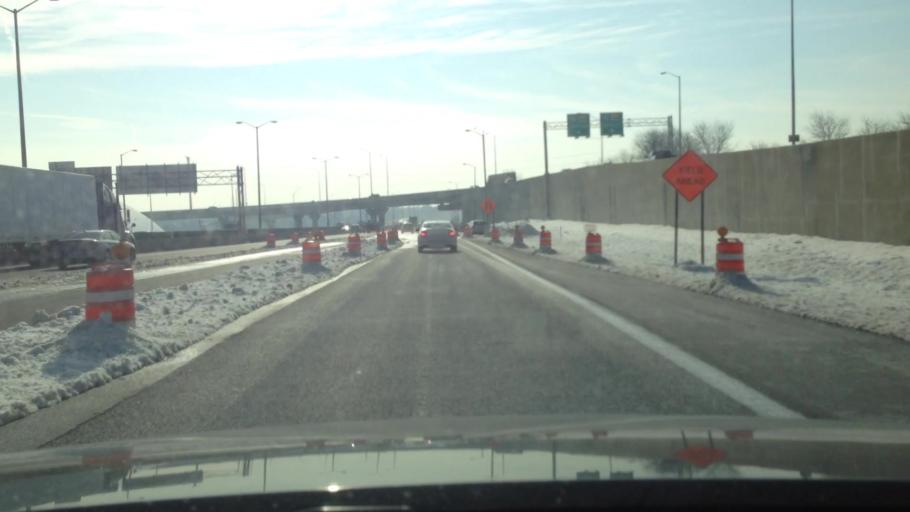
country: US
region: Illinois
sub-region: DuPage County
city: Downers Grove
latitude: 41.8256
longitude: -88.0287
